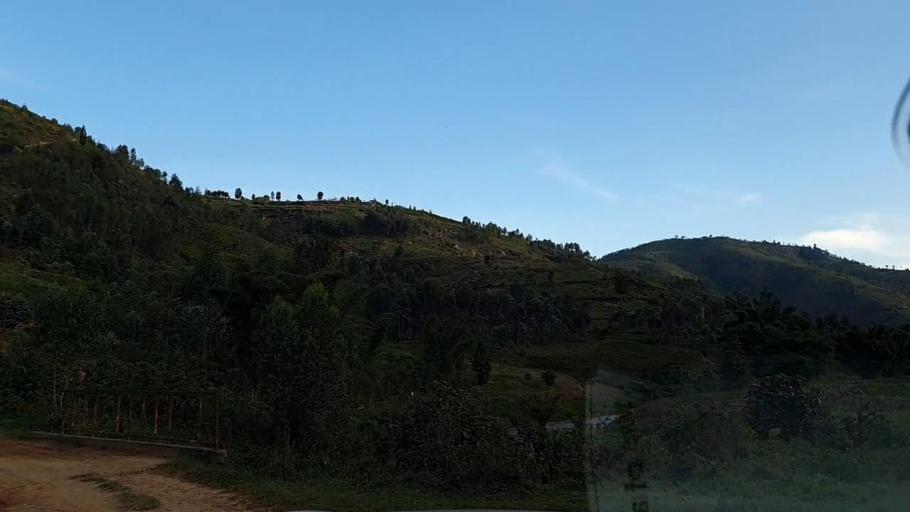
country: RW
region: Southern Province
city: Gikongoro
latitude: -2.4030
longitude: 29.5657
